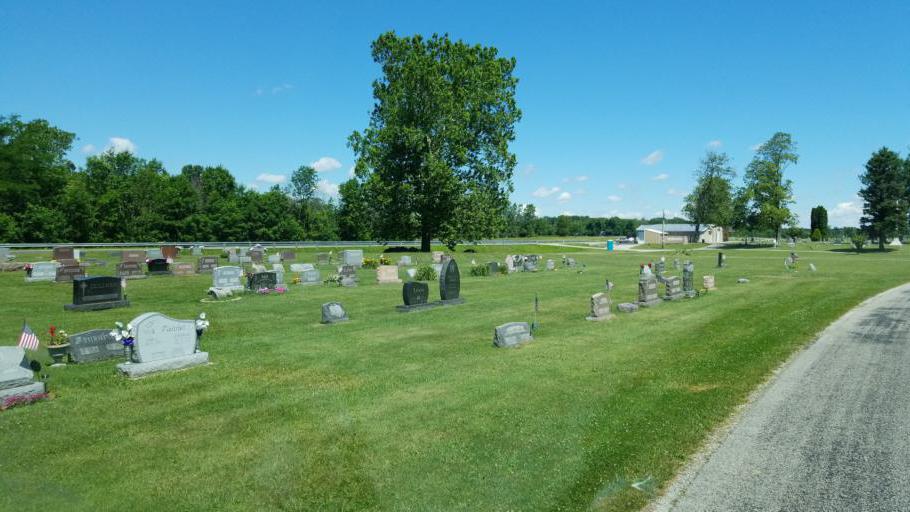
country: US
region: Ohio
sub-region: Morrow County
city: Cardington
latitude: 40.6318
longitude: -82.9588
